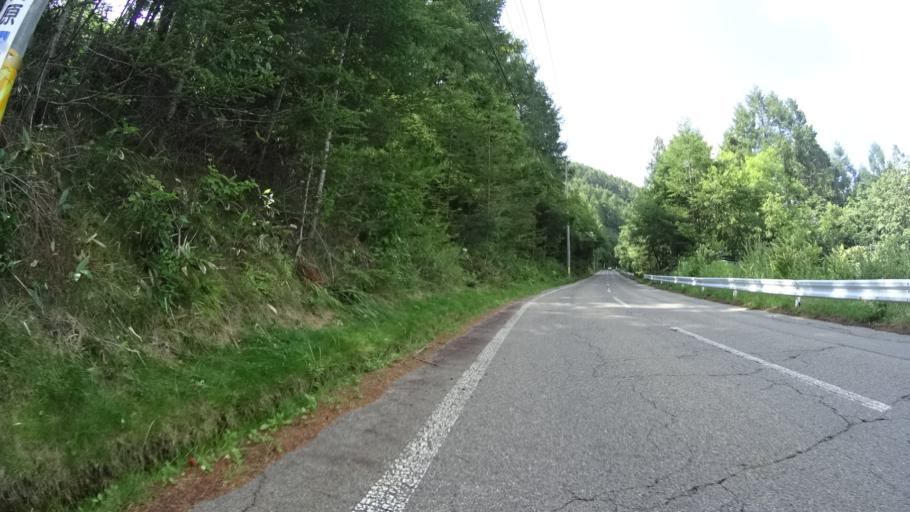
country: JP
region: Nagano
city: Saku
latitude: 36.0493
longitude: 138.4056
